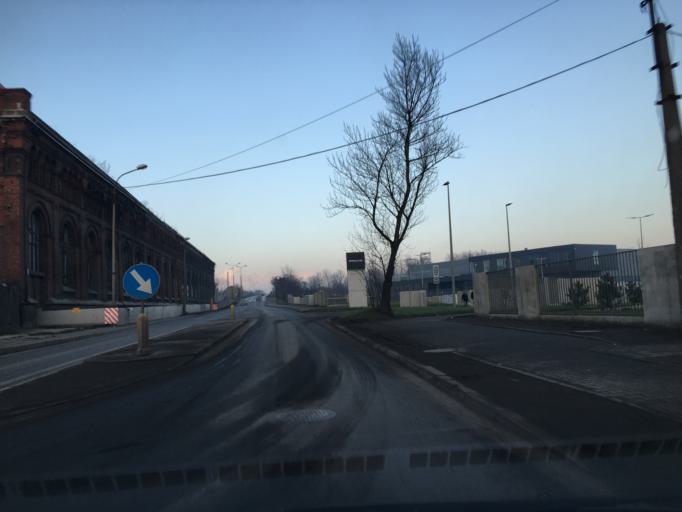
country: PL
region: Silesian Voivodeship
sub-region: Bytom
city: Bytom
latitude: 50.3416
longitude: 18.8716
